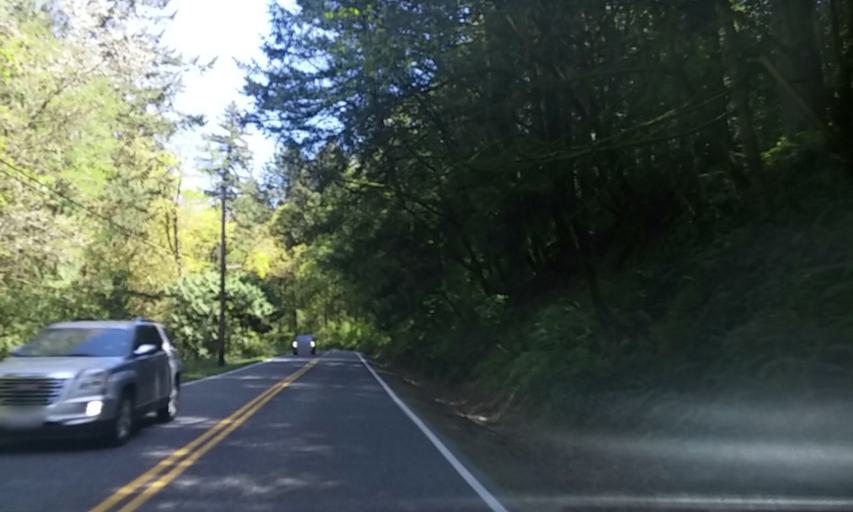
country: US
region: Oregon
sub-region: Washington County
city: West Haven
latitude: 45.5302
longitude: -122.7587
